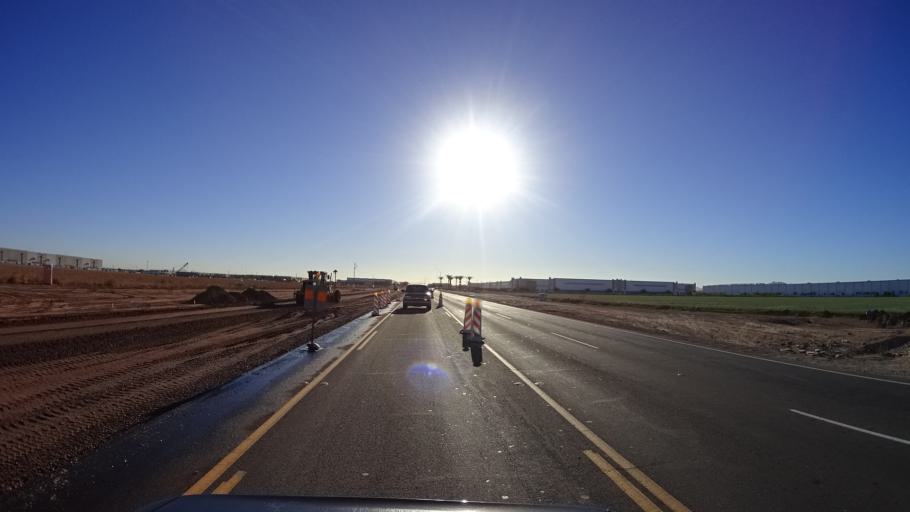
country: US
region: Arizona
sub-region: Maricopa County
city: Tolleson
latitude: 33.4371
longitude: -112.2291
